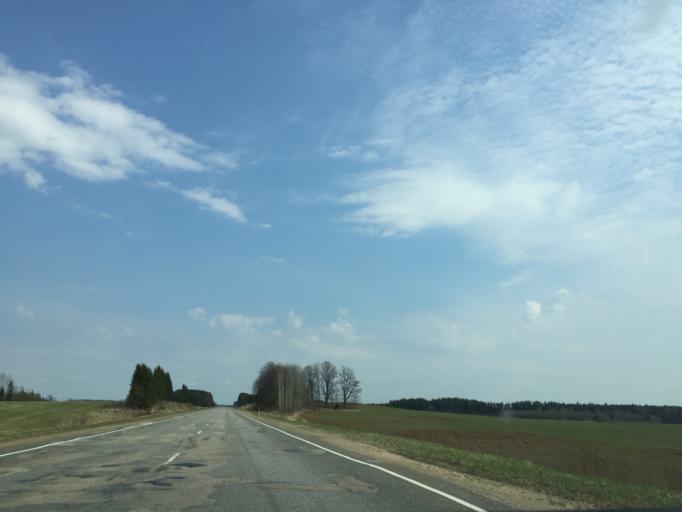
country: LV
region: Apes Novads
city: Ape
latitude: 57.4657
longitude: 26.4248
